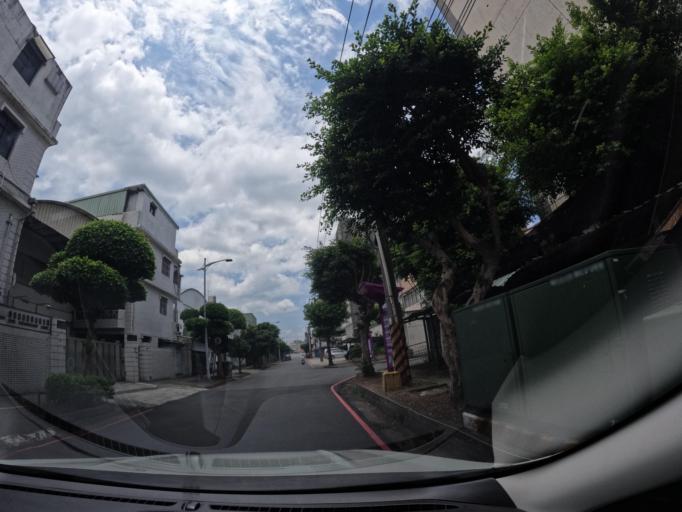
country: TW
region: Taipei
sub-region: Taipei
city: Banqiao
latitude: 24.9698
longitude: 121.4300
